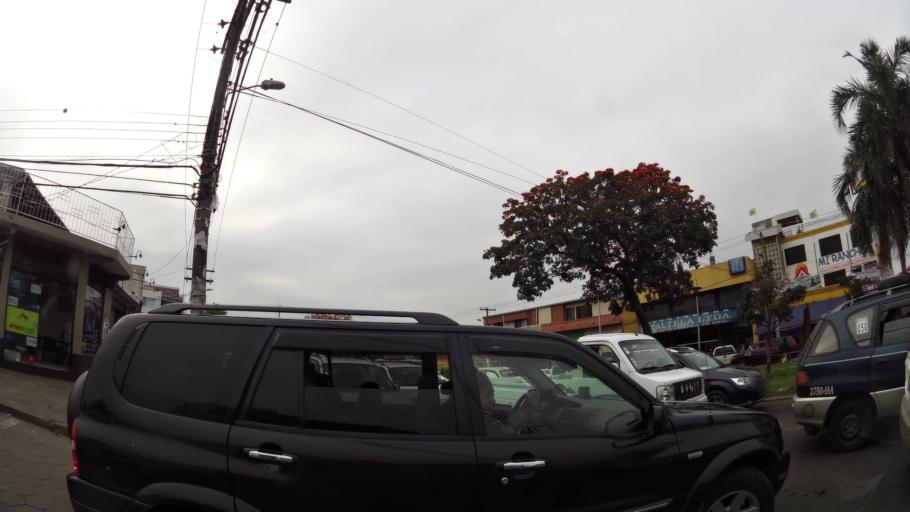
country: BO
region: Santa Cruz
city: Santa Cruz de la Sierra
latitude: -17.7885
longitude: -63.1881
